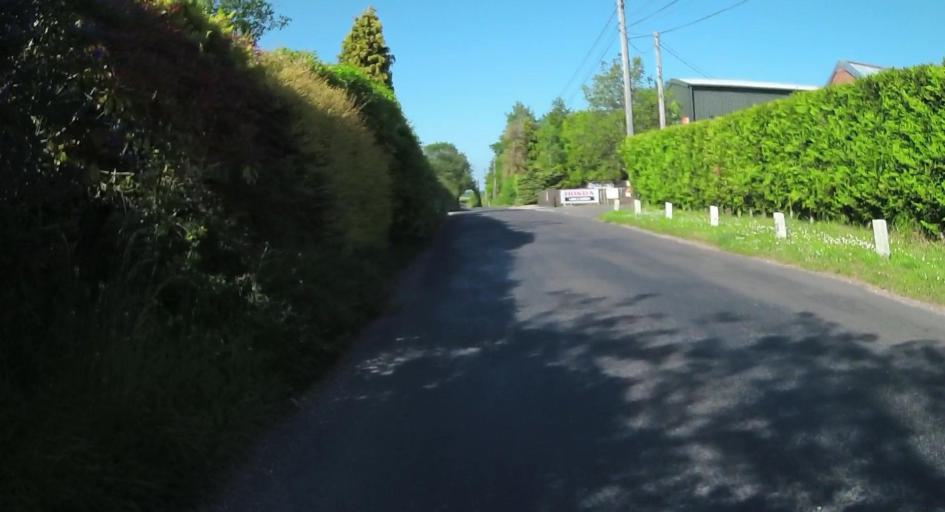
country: GB
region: England
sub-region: Hampshire
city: Kings Worthy
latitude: 51.0644
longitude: -1.2751
